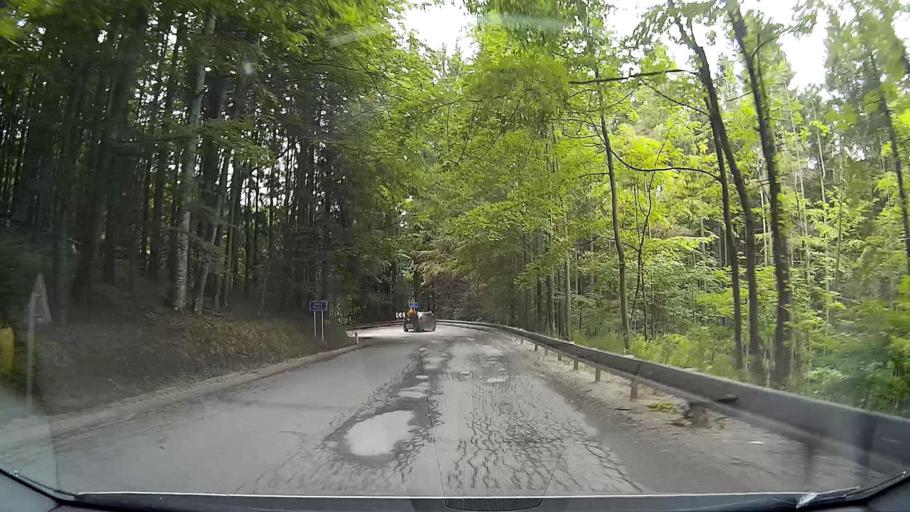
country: SK
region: Banskobystricky
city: Revuca
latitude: 48.7908
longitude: 20.1309
